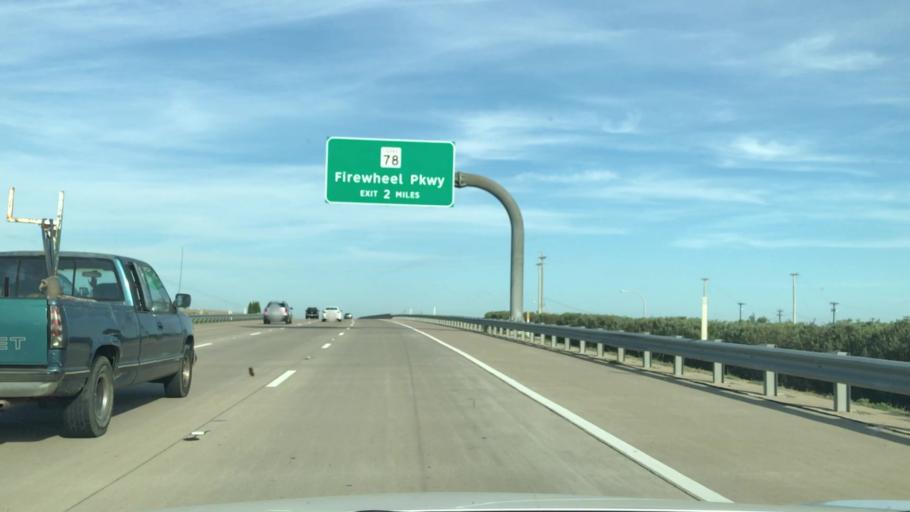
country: US
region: Texas
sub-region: Dallas County
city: Sachse
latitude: 32.9504
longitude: -96.5687
